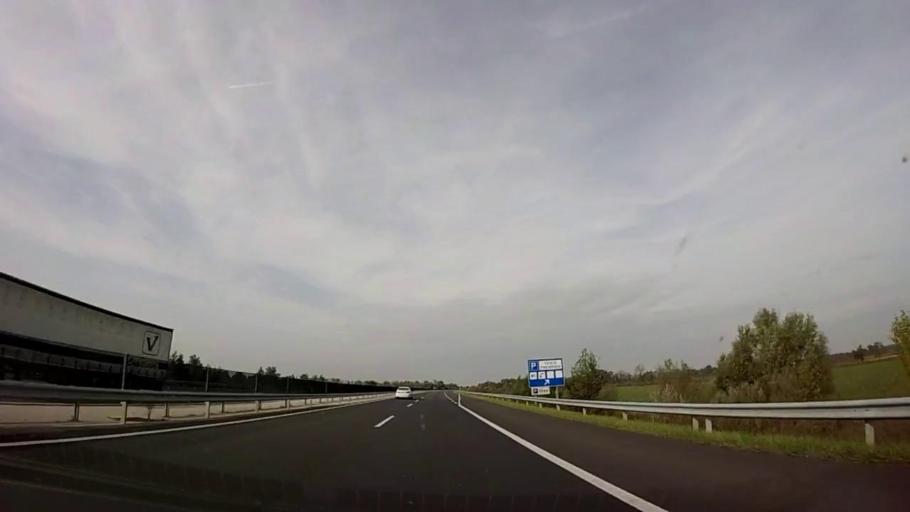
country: HU
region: Somogy
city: Balatonfenyves
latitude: 46.6983
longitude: 17.5208
